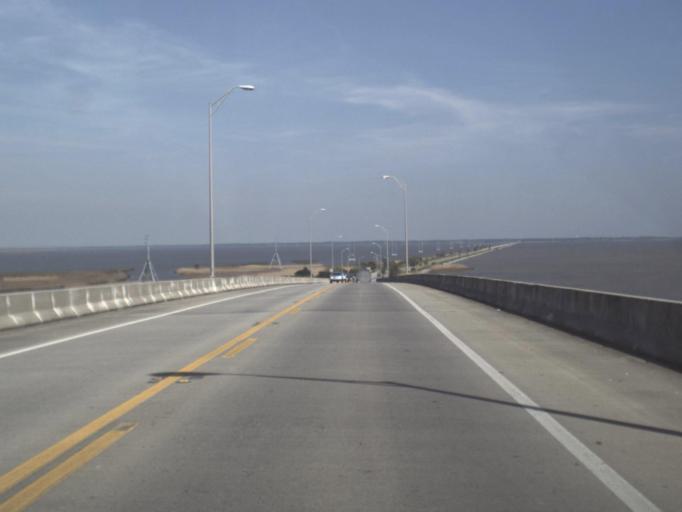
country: US
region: Florida
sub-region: Franklin County
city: Apalachicola
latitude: 29.7242
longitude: -84.9781
